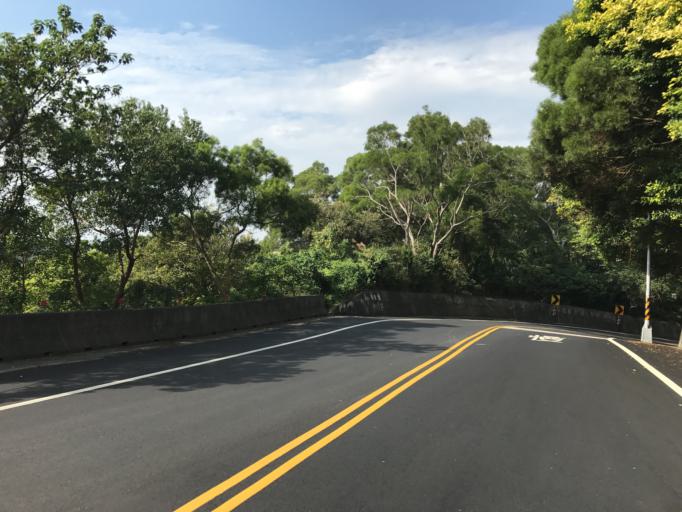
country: TW
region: Taiwan
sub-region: Hsinchu
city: Hsinchu
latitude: 24.7881
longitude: 120.9568
